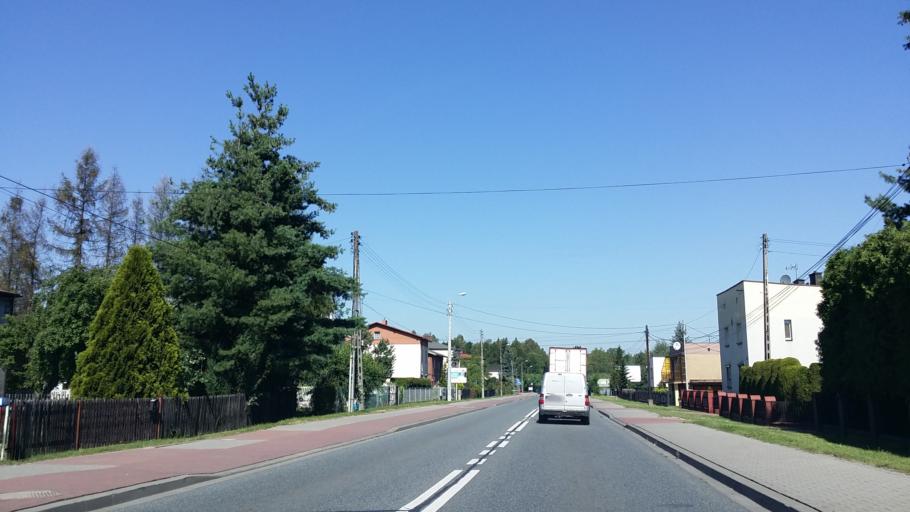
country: PL
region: Silesian Voivodeship
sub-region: Powiat bierunsko-ledzinski
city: Imielin
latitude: 50.1561
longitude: 19.1787
